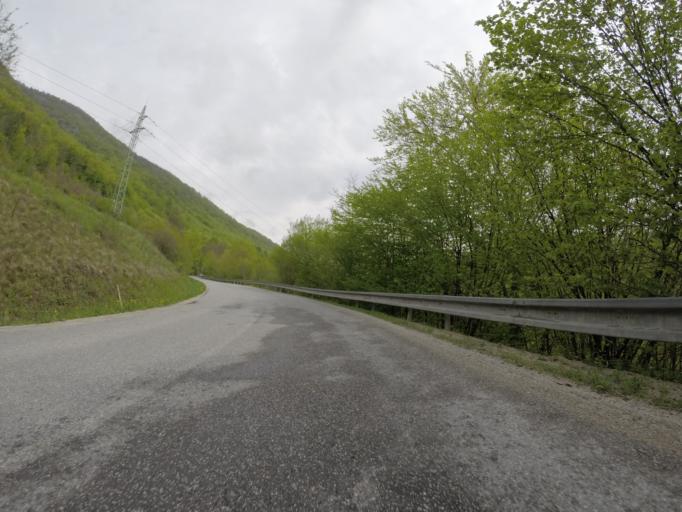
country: SK
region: Banskobystricky
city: Tisovec
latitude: 48.6929
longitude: 19.9728
